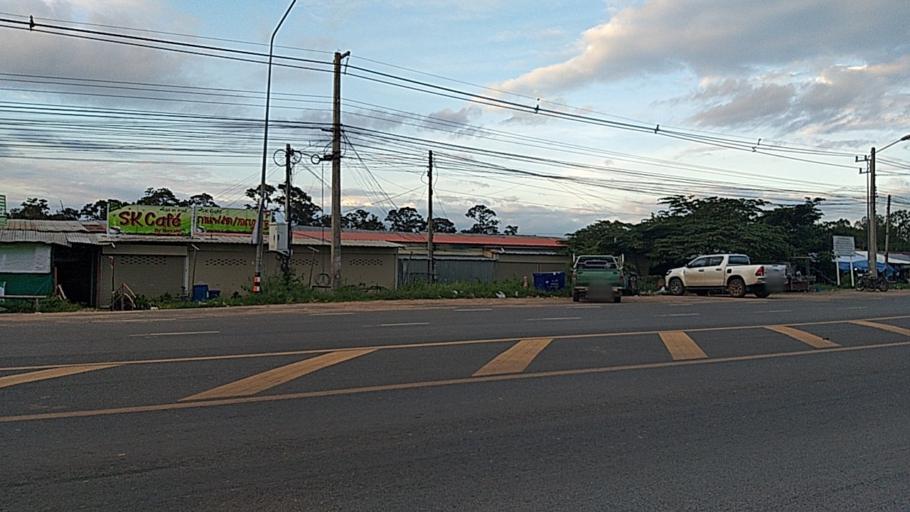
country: TH
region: Surin
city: Kap Choeng
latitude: 14.4539
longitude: 103.6874
